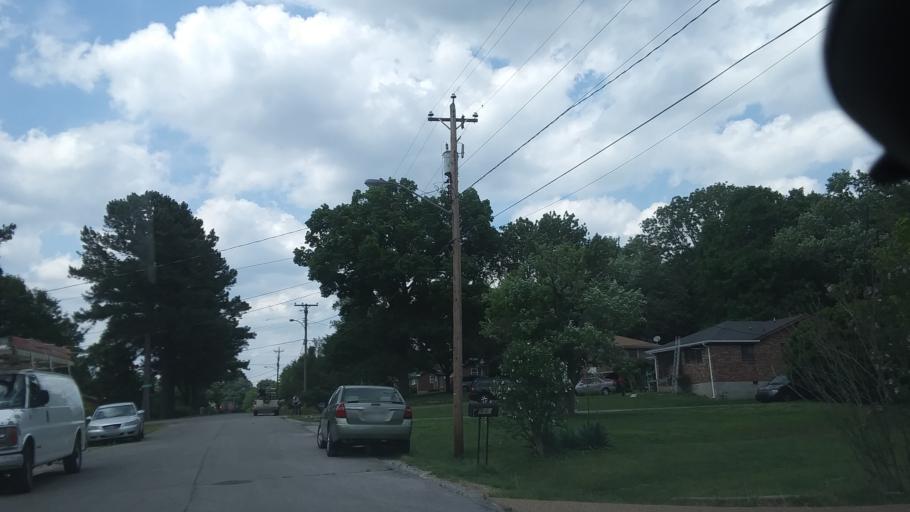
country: US
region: Tennessee
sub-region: Rutherford County
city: La Vergne
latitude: 36.0974
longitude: -86.6644
